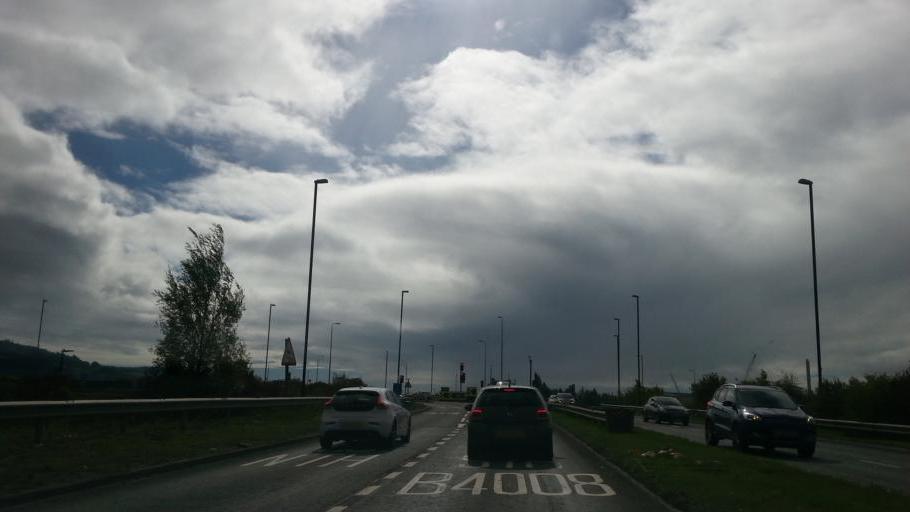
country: GB
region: England
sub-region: Gloucestershire
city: Stonehouse
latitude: 51.7999
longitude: -2.2894
